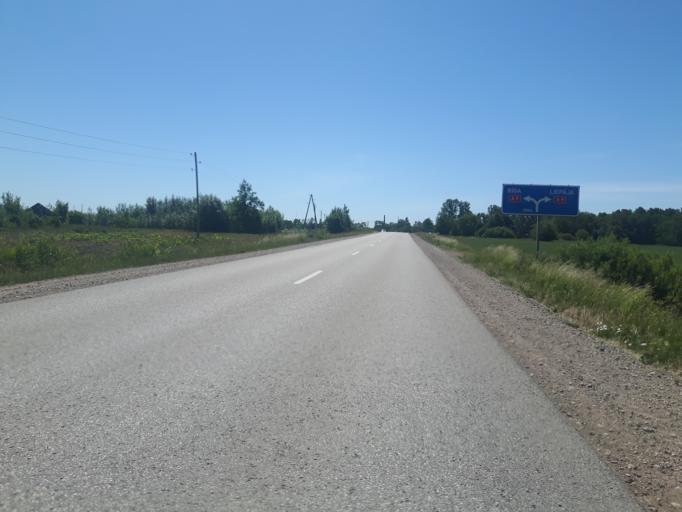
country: LV
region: Durbe
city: Liegi
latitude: 56.5690
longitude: 21.2710
